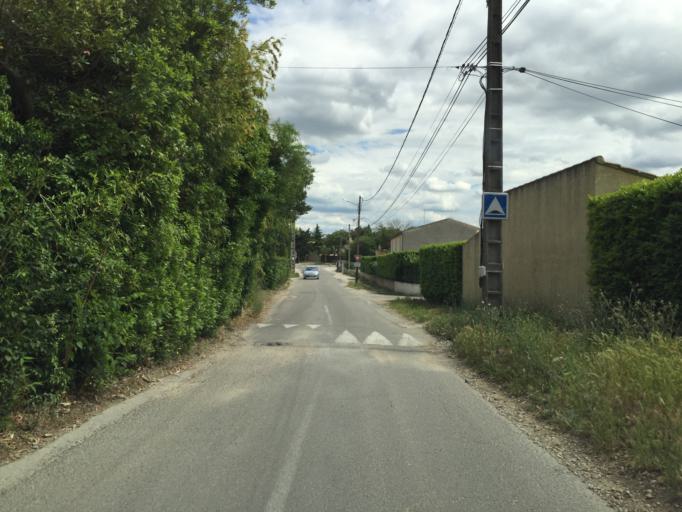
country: FR
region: Provence-Alpes-Cote d'Azur
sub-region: Departement du Vaucluse
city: Sorgues
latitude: 44.0188
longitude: 4.8627
